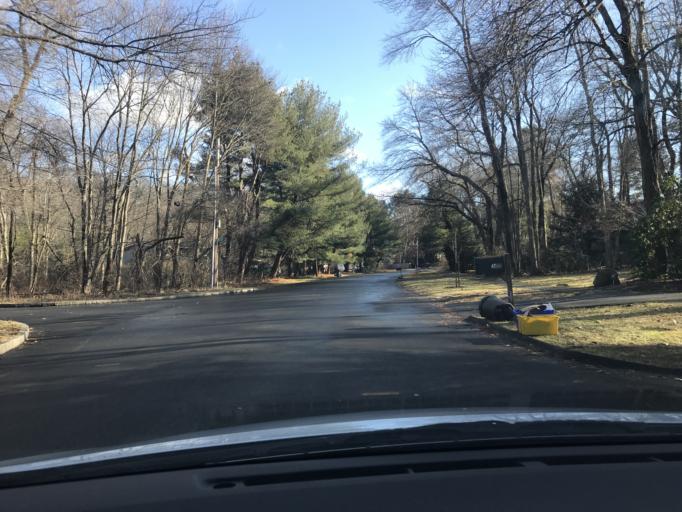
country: US
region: Massachusetts
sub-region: Middlesex County
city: Lexington
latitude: 42.4725
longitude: -71.2303
